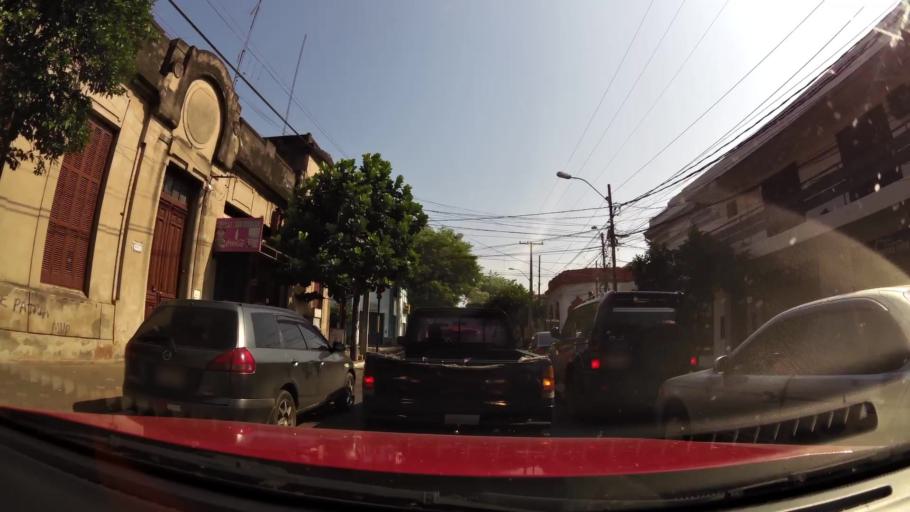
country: PY
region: Asuncion
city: Asuncion
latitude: -25.2928
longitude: -57.6300
